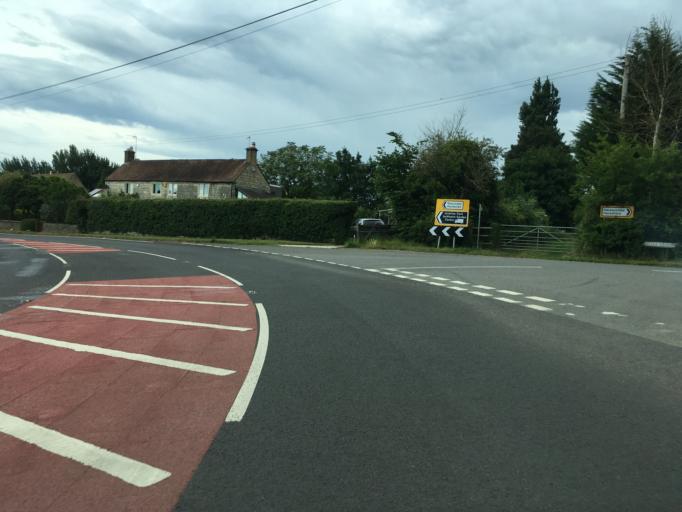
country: GB
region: England
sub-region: Gloucestershire
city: Stonehouse
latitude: 51.7806
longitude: -2.2875
